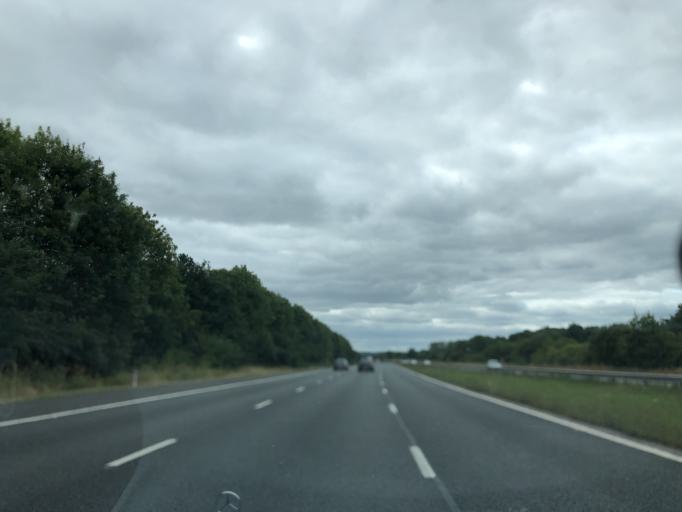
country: GB
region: England
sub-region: Oxfordshire
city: Wheatley
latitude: 51.7878
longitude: -1.0873
